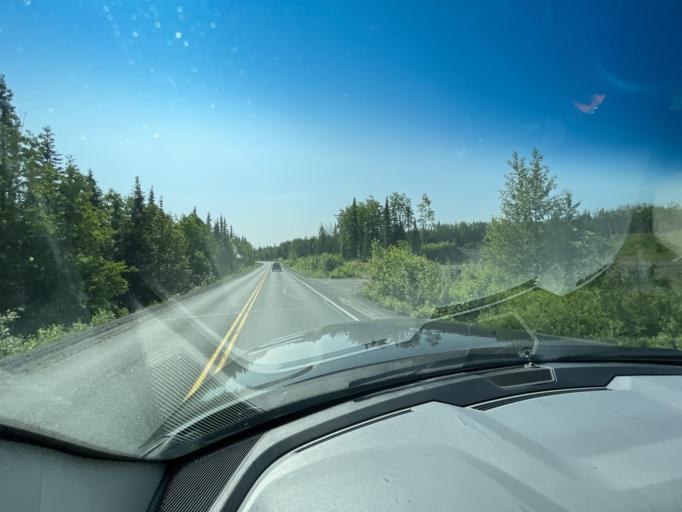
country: US
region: Alaska
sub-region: Kenai Peninsula Borough
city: Cohoe
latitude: 60.3019
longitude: -151.2843
